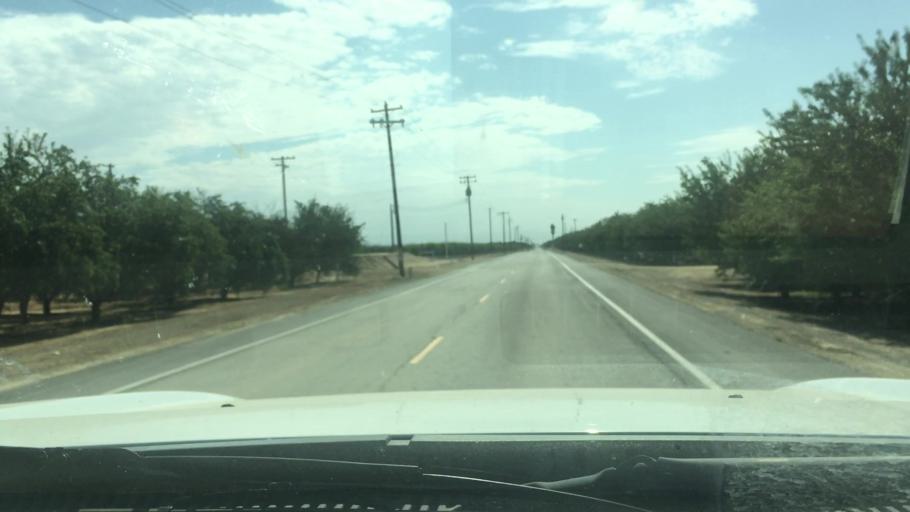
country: US
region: California
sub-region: Kern County
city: Wasco
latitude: 35.5577
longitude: -119.4573
